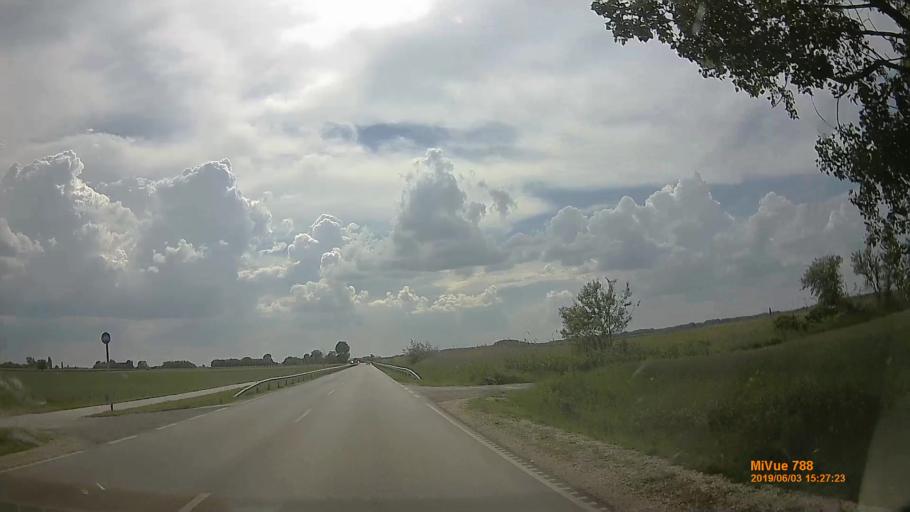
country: HU
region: Bacs-Kiskun
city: Soltvadkert
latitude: 46.5990
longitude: 19.4256
